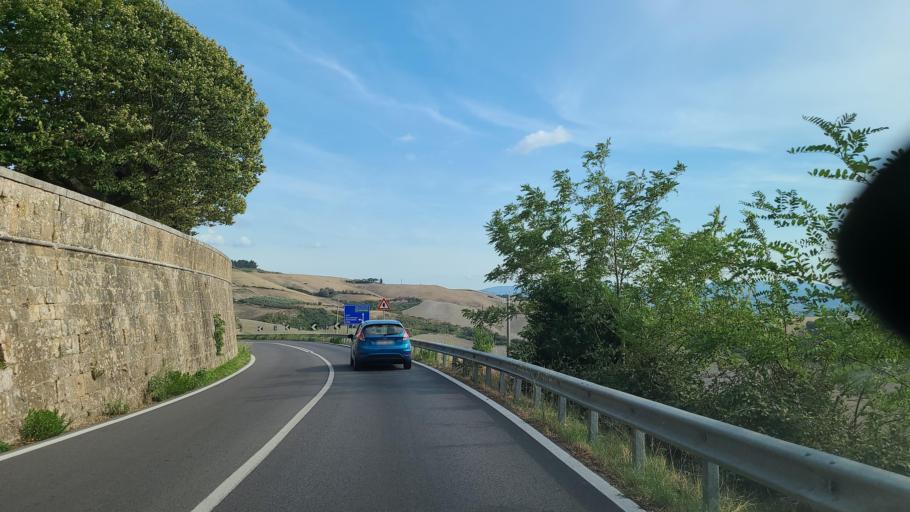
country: IT
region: Tuscany
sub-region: Province of Pisa
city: Volterra
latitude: 43.3933
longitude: 10.8938
